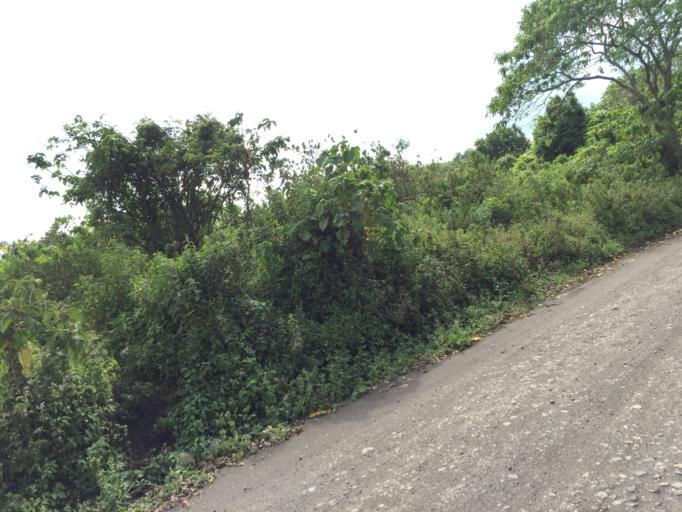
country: TZ
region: Arusha
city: Usa River
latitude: -3.3053
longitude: 36.8769
